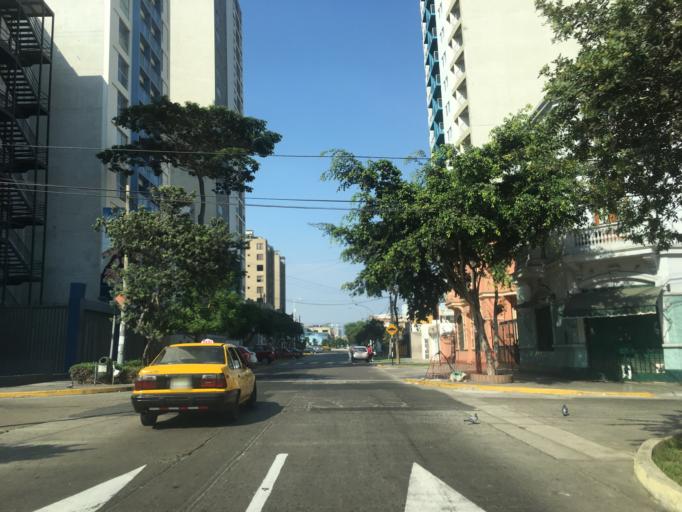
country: PE
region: Lima
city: Lima
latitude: -12.0729
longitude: -77.0327
